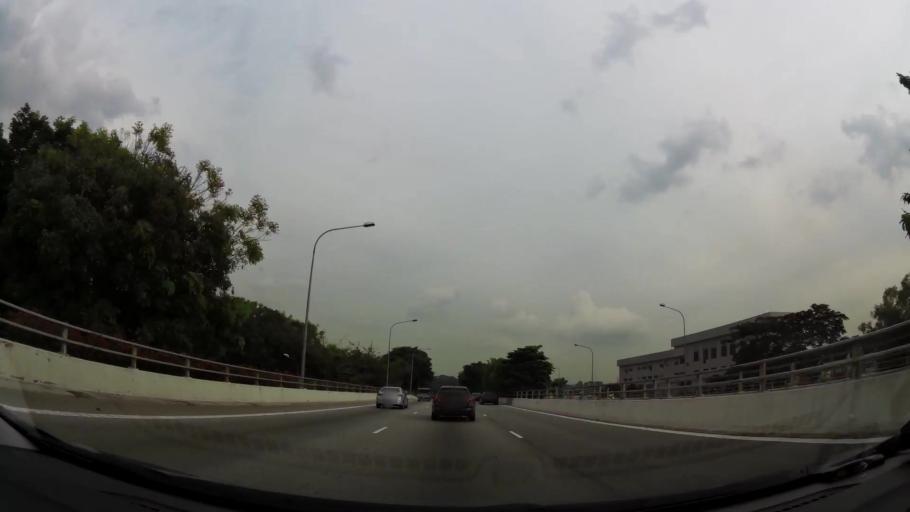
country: MY
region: Johor
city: Johor Bahru
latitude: 1.4226
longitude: 103.7951
